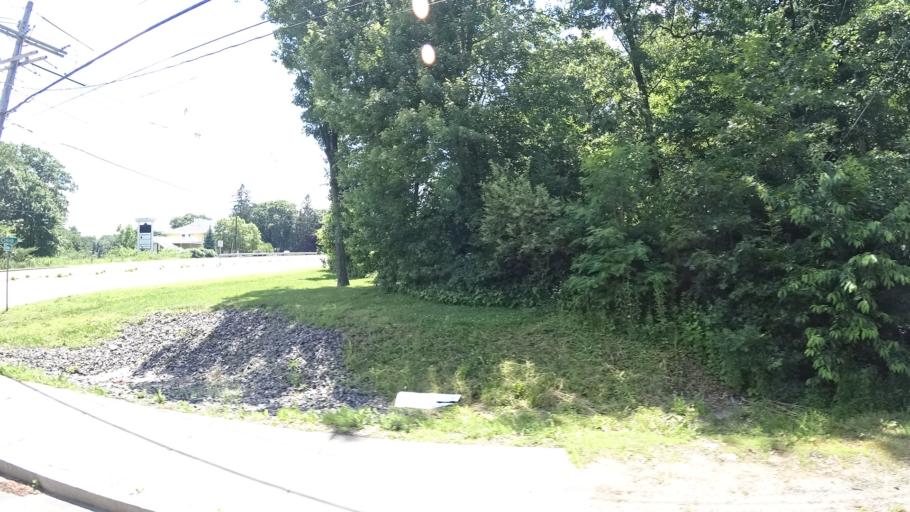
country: US
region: Massachusetts
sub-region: Norfolk County
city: Westwood
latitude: 42.2422
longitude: -71.2093
